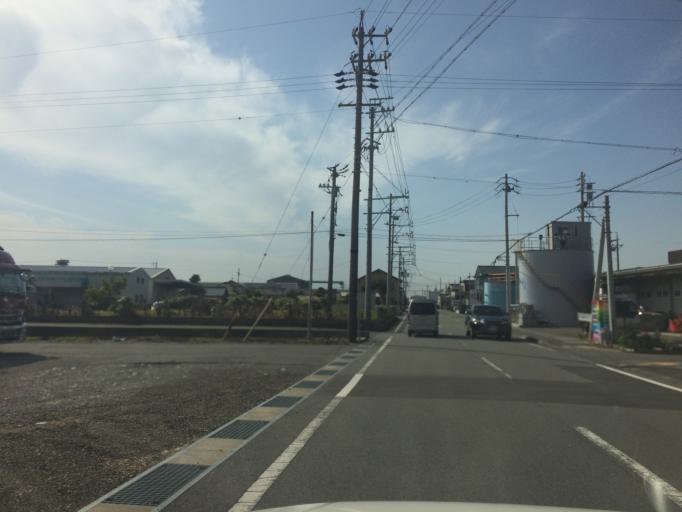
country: JP
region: Shizuoka
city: Fujieda
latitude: 34.7912
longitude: 138.2897
